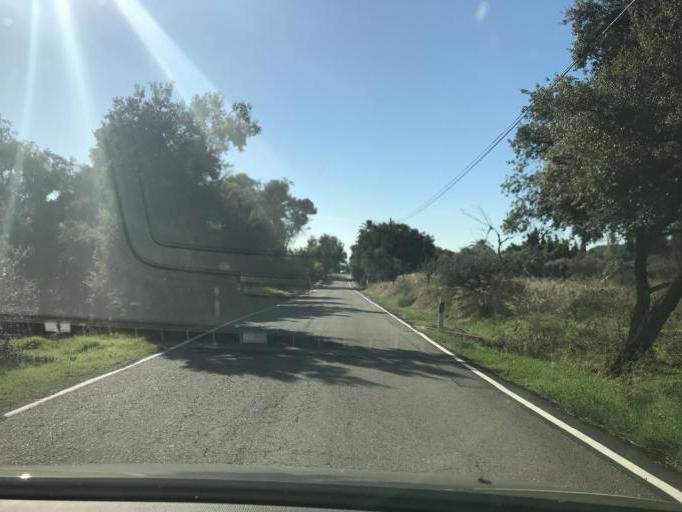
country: ES
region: Andalusia
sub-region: Province of Cordoba
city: Cordoba
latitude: 37.9323
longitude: -4.8031
